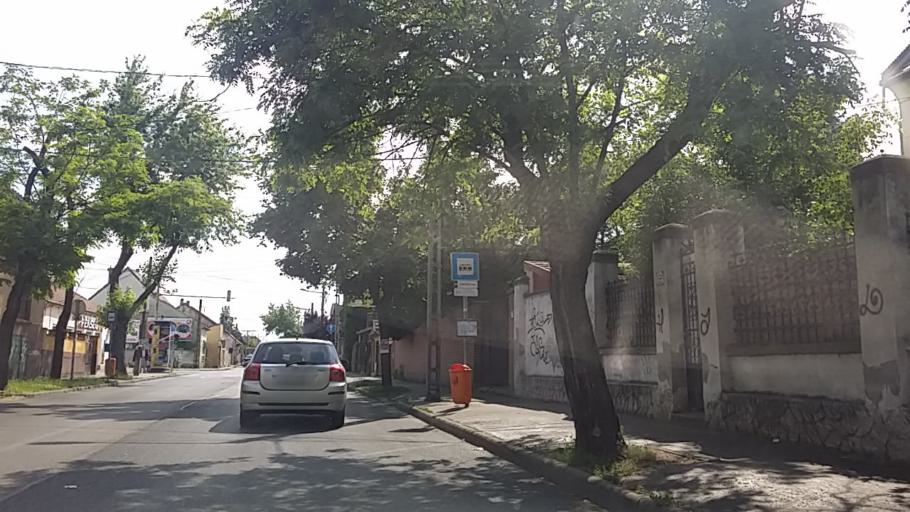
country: HU
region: Budapest
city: Budapest XX. keruelet
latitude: 47.4408
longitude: 19.1184
